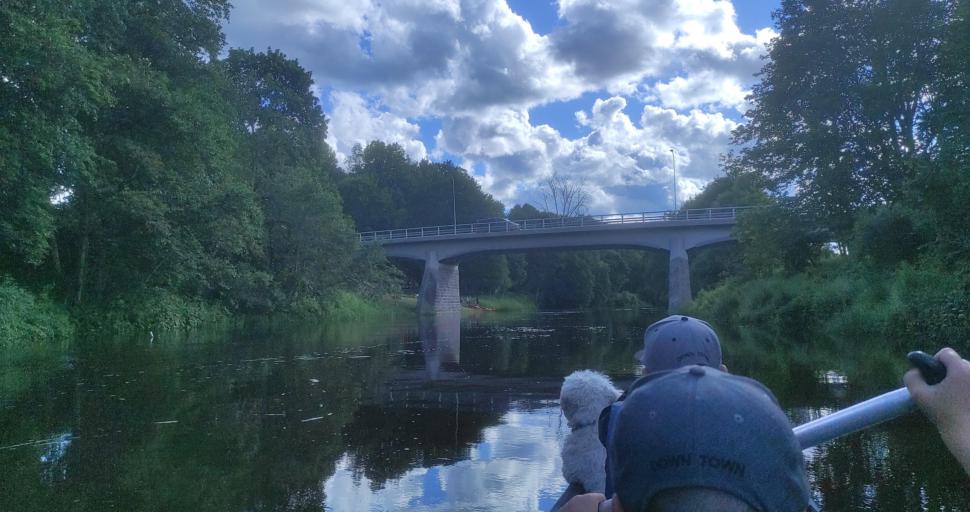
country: LV
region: Talsu Rajons
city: Stende
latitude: 57.0709
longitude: 22.2933
